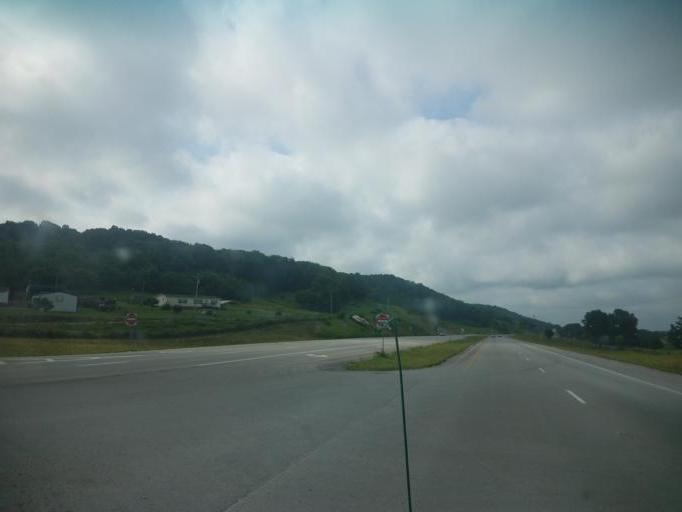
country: US
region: Kentucky
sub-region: Clinton County
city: Albany
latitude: 36.7414
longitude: -85.1346
